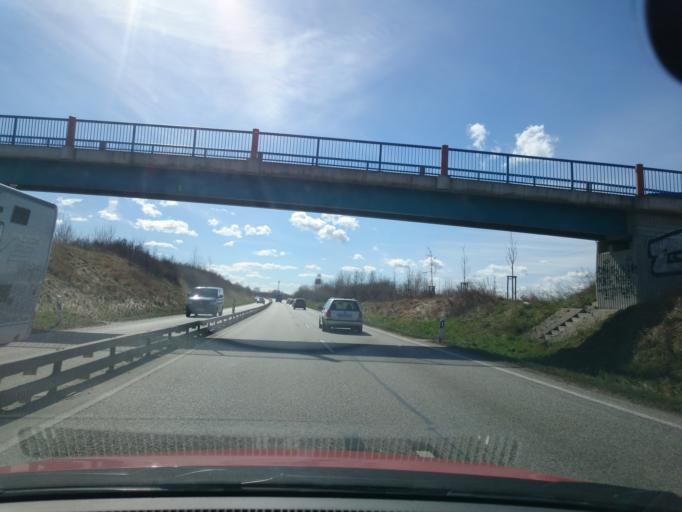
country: DE
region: Mecklenburg-Vorpommern
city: Bentwisch
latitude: 54.1172
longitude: 12.1972
